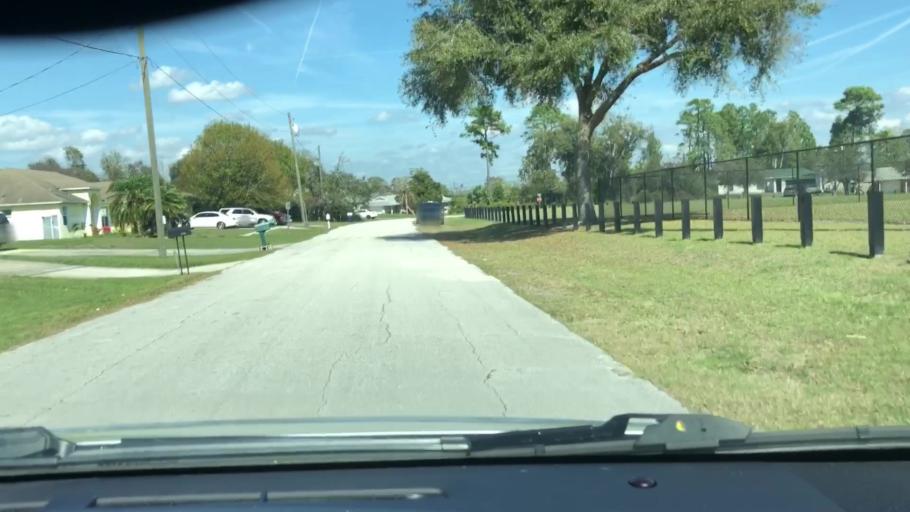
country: US
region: Florida
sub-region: Volusia County
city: Deltona
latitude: 28.8870
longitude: -81.2310
